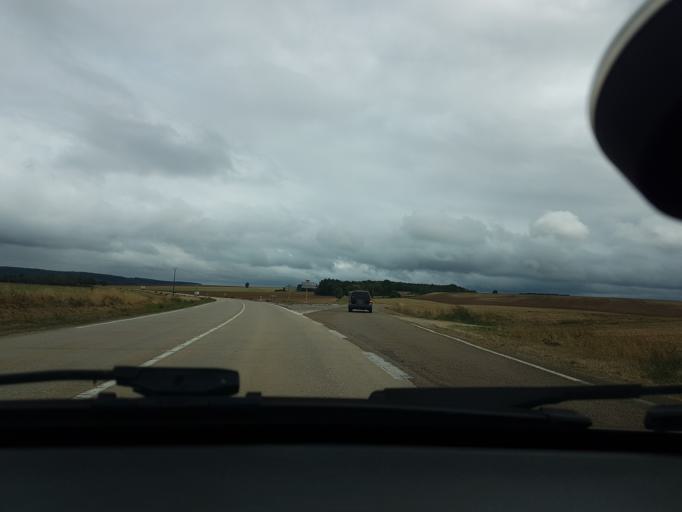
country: FR
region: Bourgogne
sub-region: Departement de l'Yonne
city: Saint-Bris-le-Vineux
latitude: 47.6913
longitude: 3.6480
